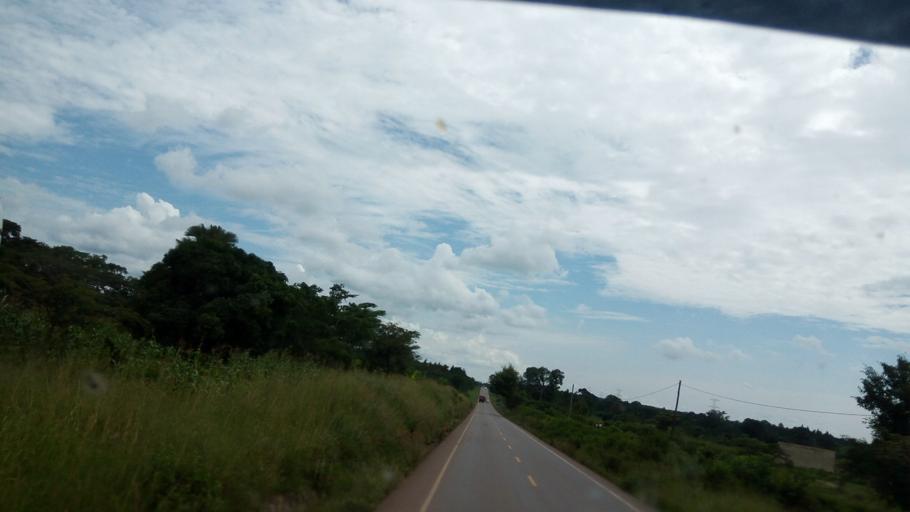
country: UG
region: Central Region
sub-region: Nakasongola District
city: Nakasongola
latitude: 1.1686
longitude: 32.4633
